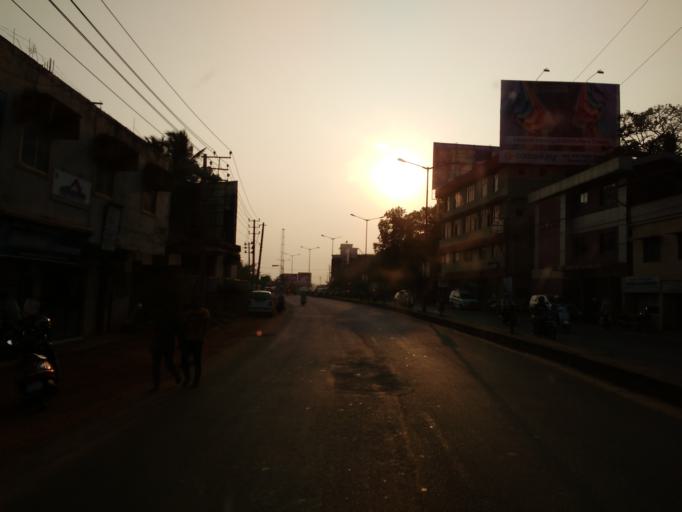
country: IN
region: Karnataka
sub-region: Dakshina Kannada
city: Mangalore
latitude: 12.8846
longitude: 74.8654
